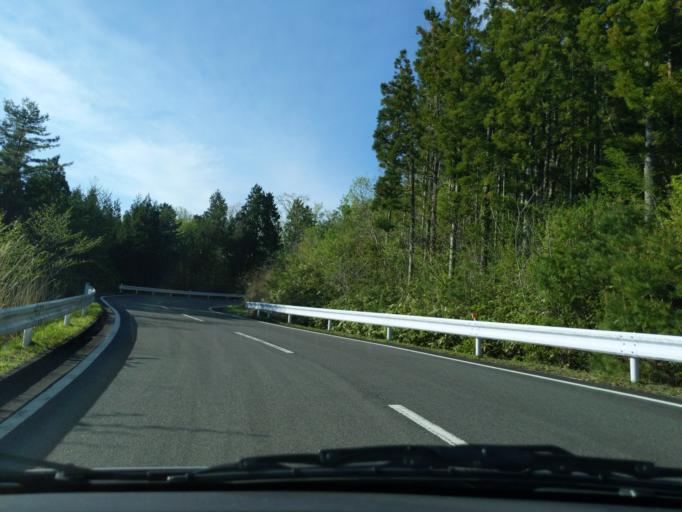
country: JP
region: Iwate
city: Ichinoseki
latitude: 38.8955
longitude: 140.8605
